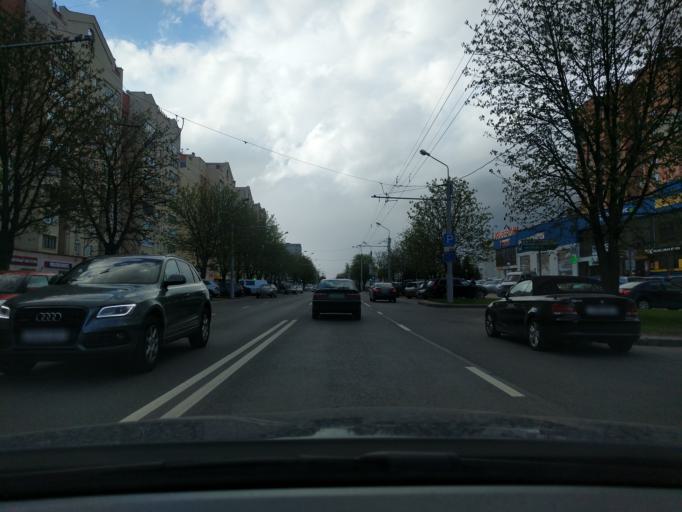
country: BY
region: Minsk
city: Novoye Medvezhino
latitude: 53.9053
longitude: 27.4813
